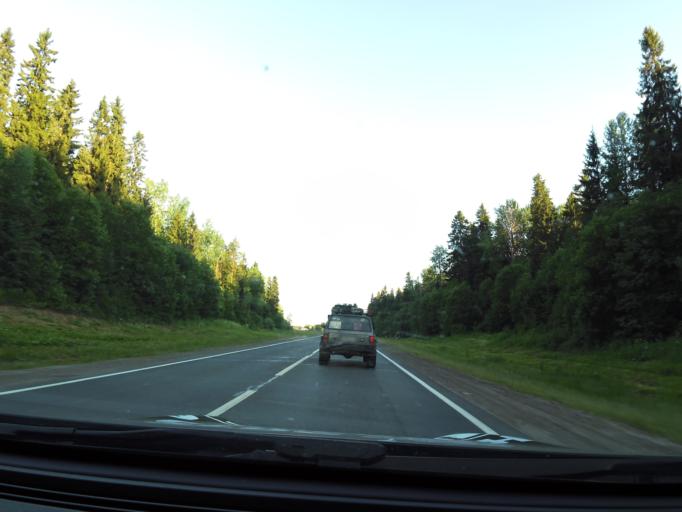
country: RU
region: Vologda
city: Gryazovets
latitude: 58.8619
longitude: 40.1986
